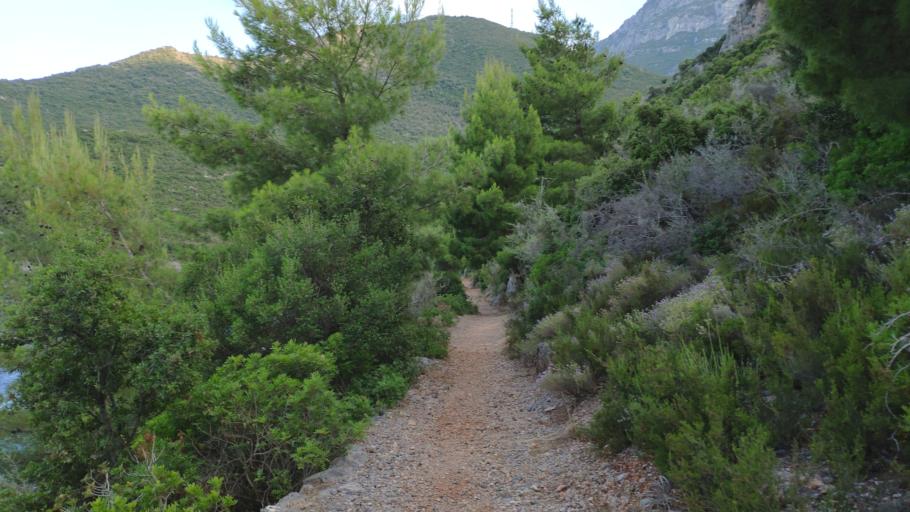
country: GR
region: Peloponnese
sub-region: Nomos Lakonias
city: Sykea
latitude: 36.9696
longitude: 22.9966
